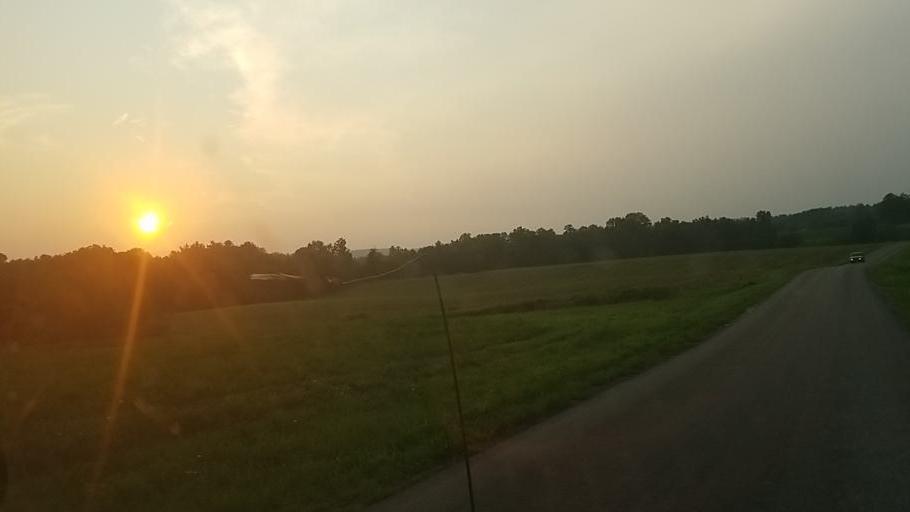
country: US
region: New York
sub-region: Montgomery County
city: Fonda
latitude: 42.9065
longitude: -74.3936
